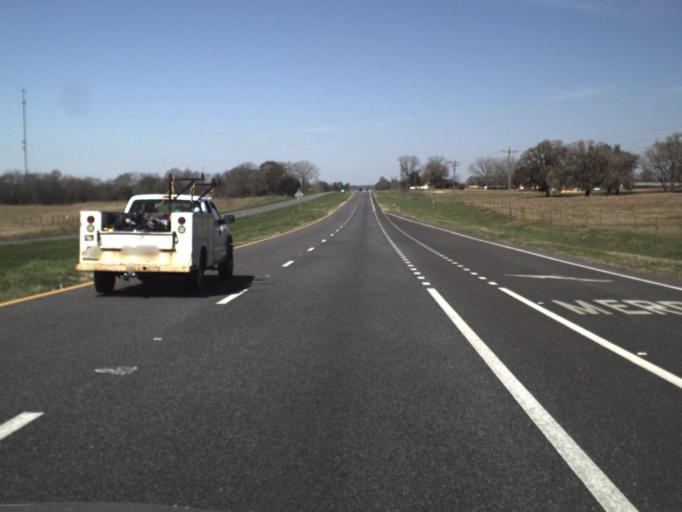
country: US
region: Florida
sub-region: Jackson County
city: Graceville
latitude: 30.8891
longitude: -85.3683
